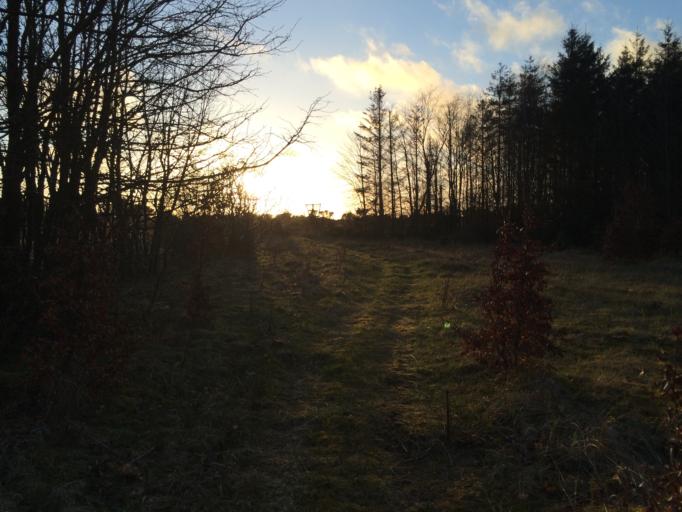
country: DK
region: Central Jutland
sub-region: Holstebro Kommune
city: Ulfborg
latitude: 56.2431
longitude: 8.4100
